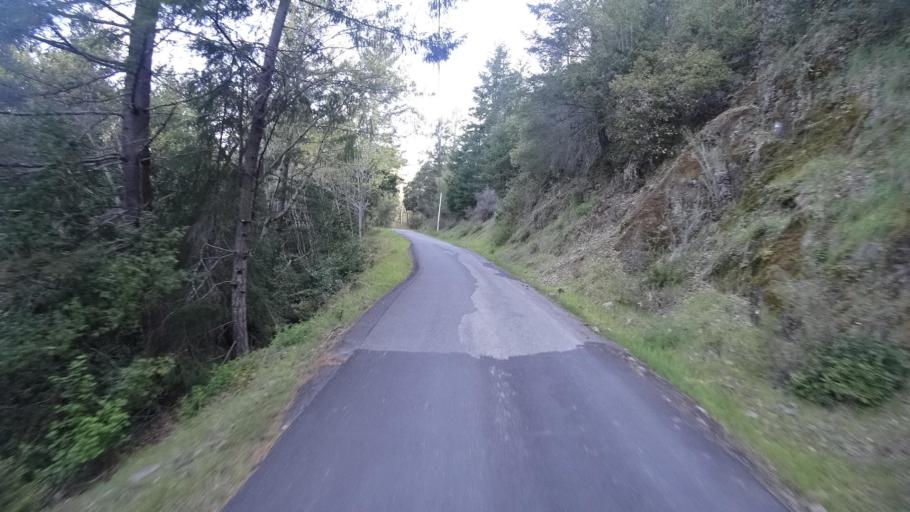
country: US
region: California
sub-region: Humboldt County
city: Blue Lake
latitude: 40.7068
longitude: -123.9366
